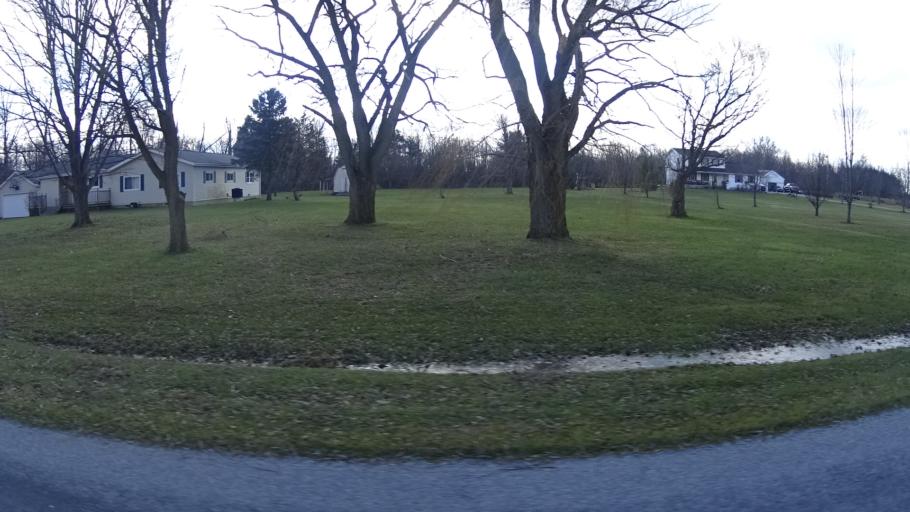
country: US
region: Ohio
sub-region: Lorain County
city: Camden
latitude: 41.2258
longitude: -82.2921
